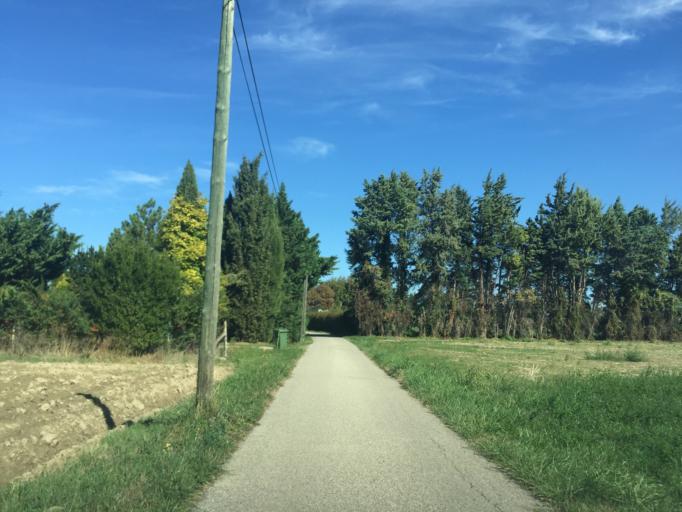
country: FR
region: Provence-Alpes-Cote d'Azur
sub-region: Departement du Vaucluse
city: Caderousse
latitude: 44.1193
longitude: 4.7233
